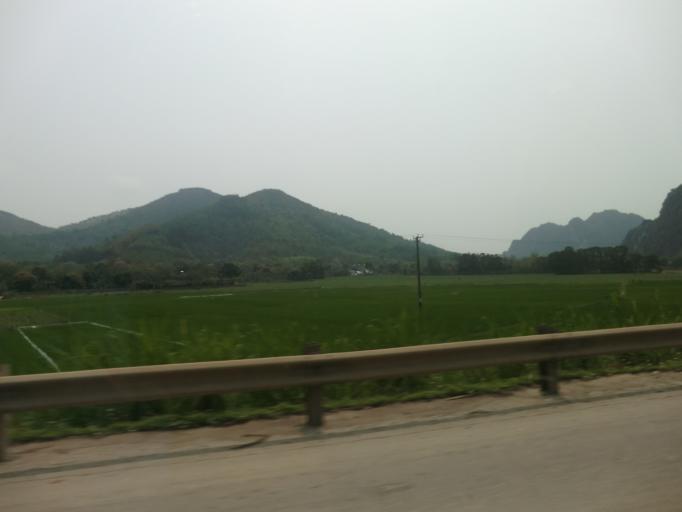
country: VN
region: Thanh Hoa
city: Thi Tran Cam Thuy
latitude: 20.2300
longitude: 105.4943
